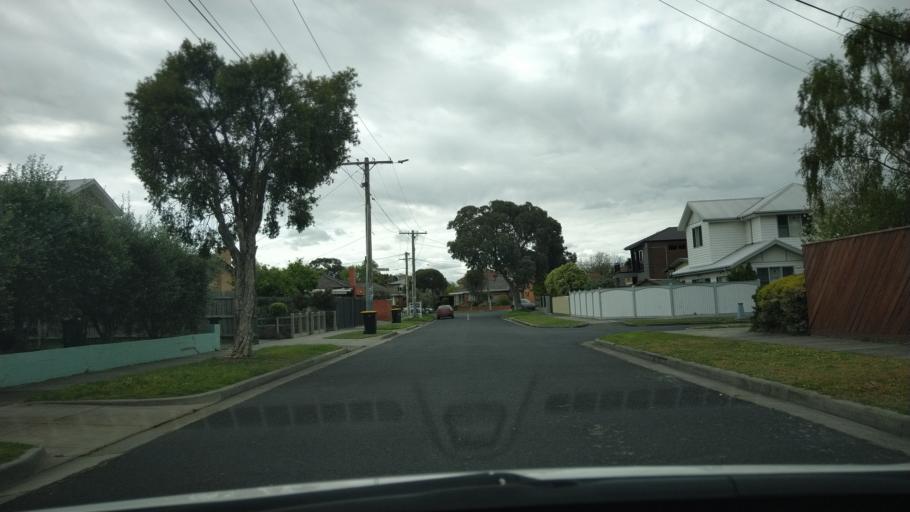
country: AU
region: Victoria
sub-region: Bayside
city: Cheltenham
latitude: -37.9612
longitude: 145.0622
